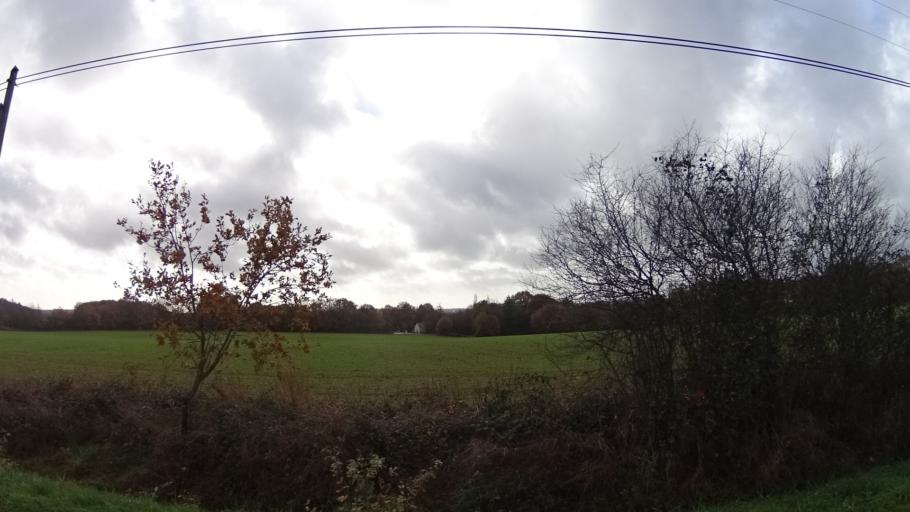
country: FR
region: Pays de la Loire
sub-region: Departement de la Loire-Atlantique
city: Fegreac
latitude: 47.5965
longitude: -2.0726
